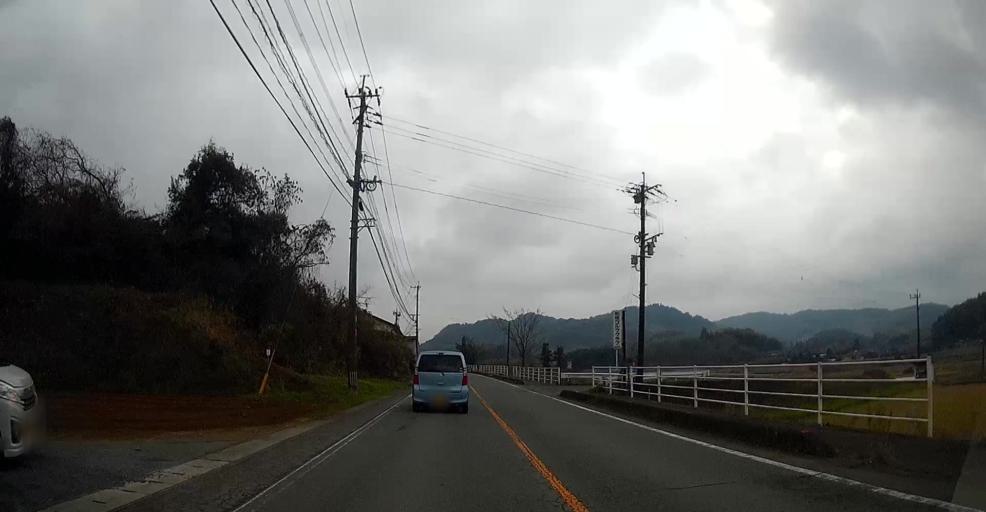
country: JP
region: Kumamoto
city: Matsubase
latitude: 32.6486
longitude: 130.7196
